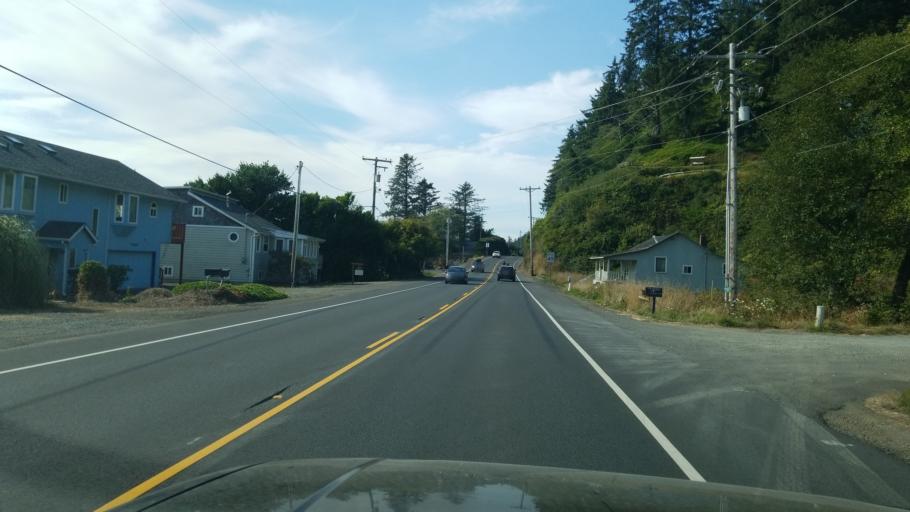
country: US
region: Oregon
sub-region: Tillamook County
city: Rockaway Beach
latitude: 45.5660
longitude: -123.9388
